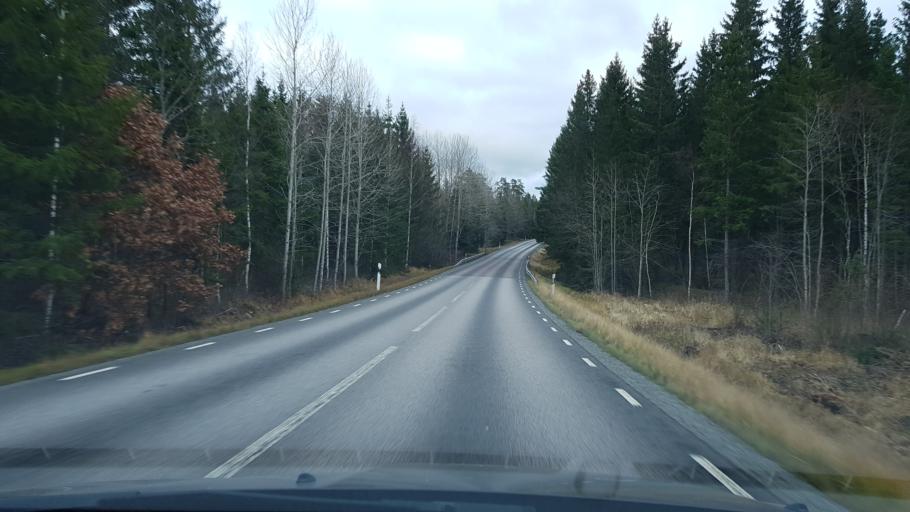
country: SE
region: Stockholm
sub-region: Norrtalje Kommun
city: Skanninge
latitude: 60.0333
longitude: 18.4452
